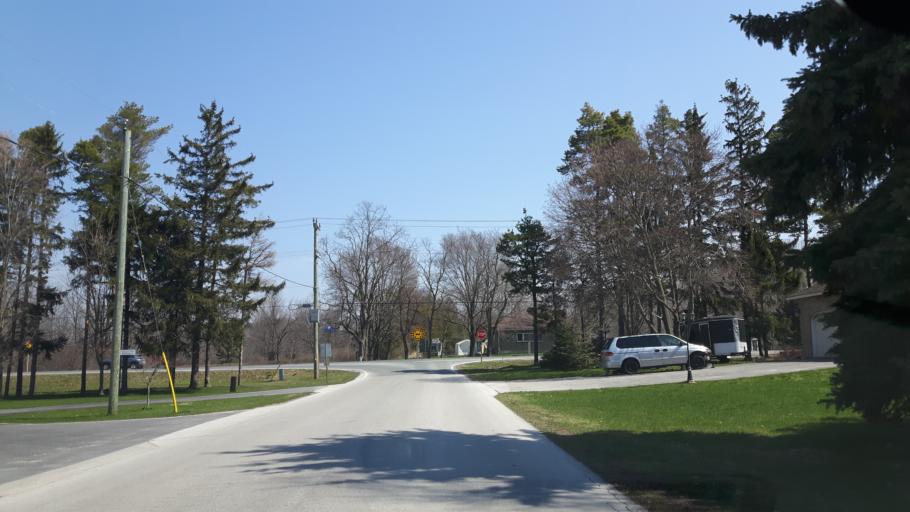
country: CA
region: Ontario
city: Goderich
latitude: 43.7271
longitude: -81.6862
